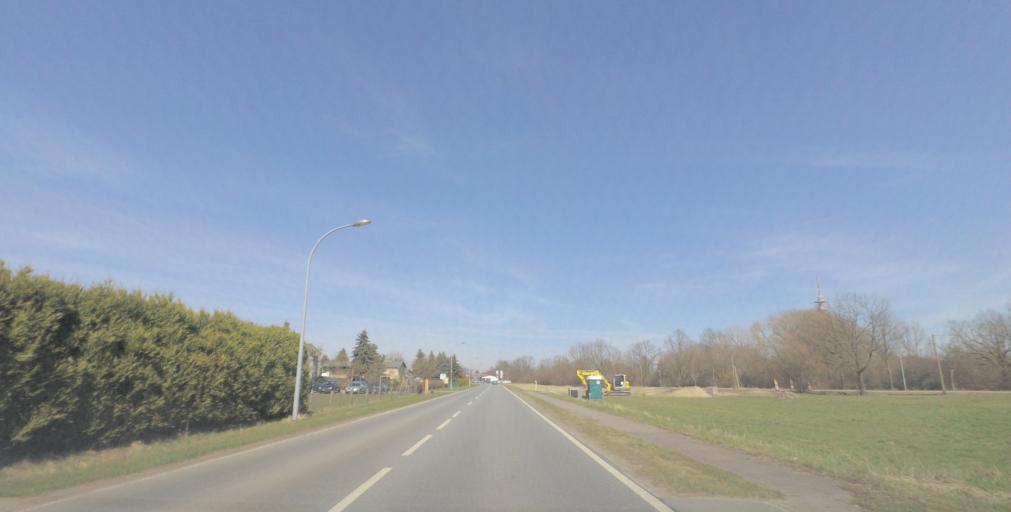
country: DE
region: Brandenburg
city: Neuruppin
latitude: 52.8871
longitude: 12.7969
